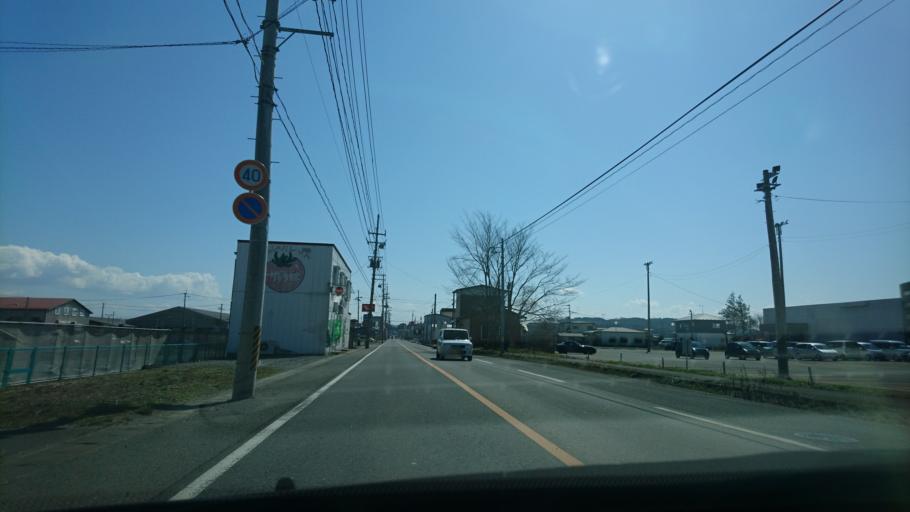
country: JP
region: Iwate
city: Ichinoseki
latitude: 38.7707
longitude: 141.1485
